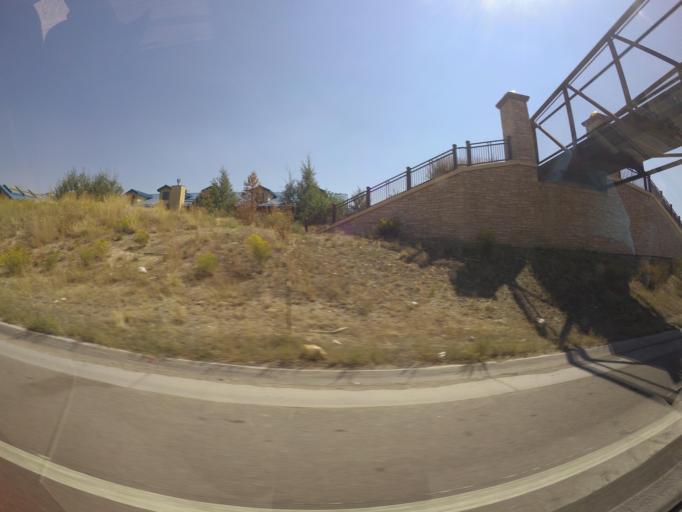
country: US
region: Colorado
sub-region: Eagle County
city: Eagle
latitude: 39.6605
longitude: -106.8264
